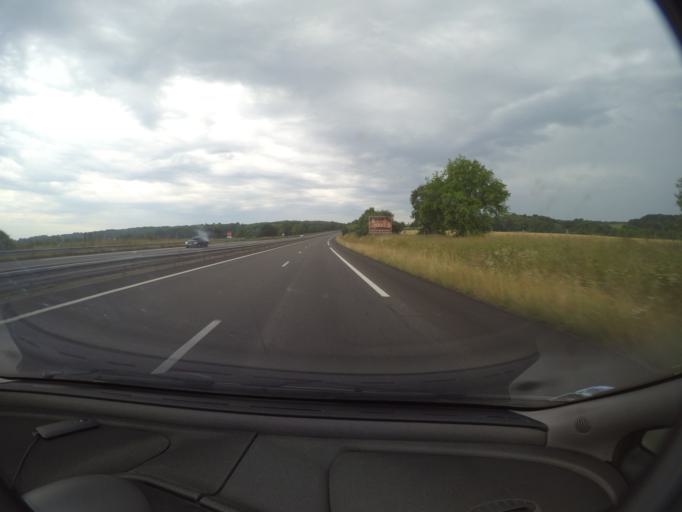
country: FR
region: Pays de la Loire
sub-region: Departement de la Loire-Atlantique
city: Mauves-sur-Loire
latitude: 47.3112
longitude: -1.4141
